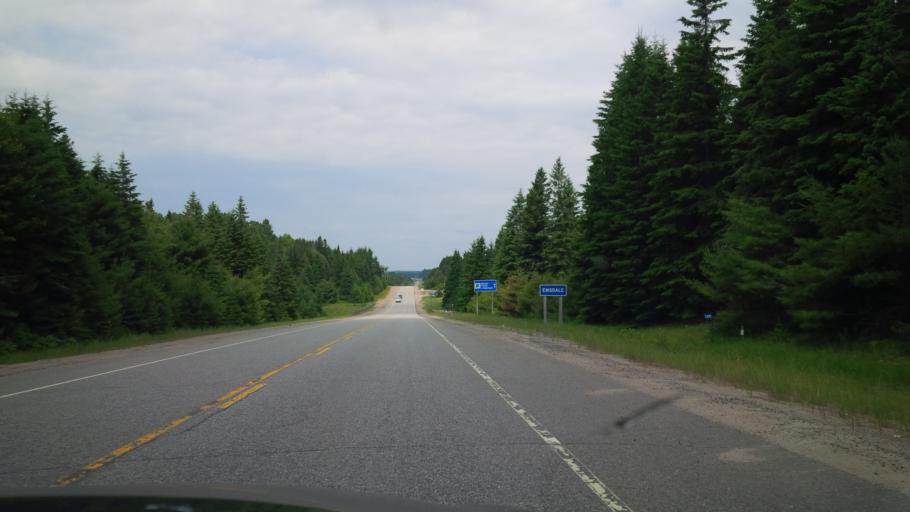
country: CA
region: Ontario
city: Huntsville
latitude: 45.5197
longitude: -79.3134
